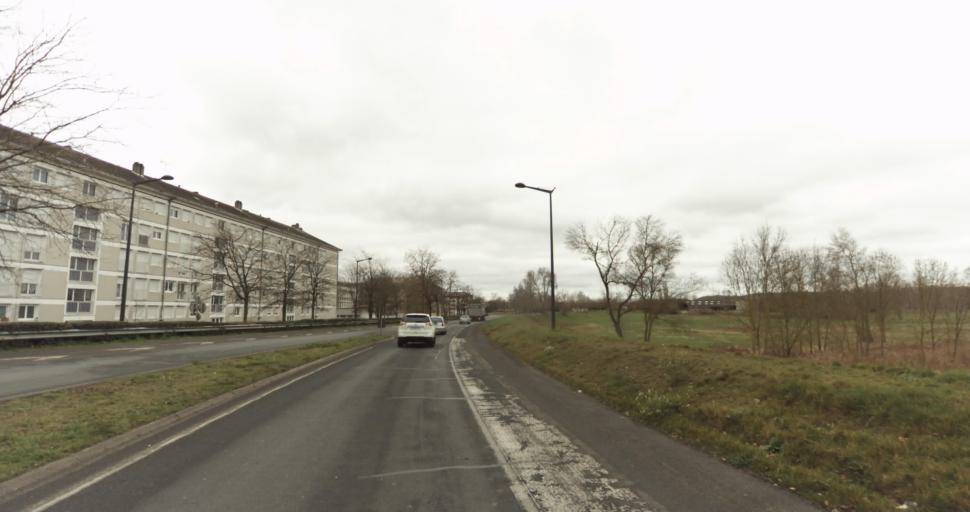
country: FR
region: Pays de la Loire
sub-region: Departement de Maine-et-Loire
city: Saumur
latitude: 47.2494
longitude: -0.0791
